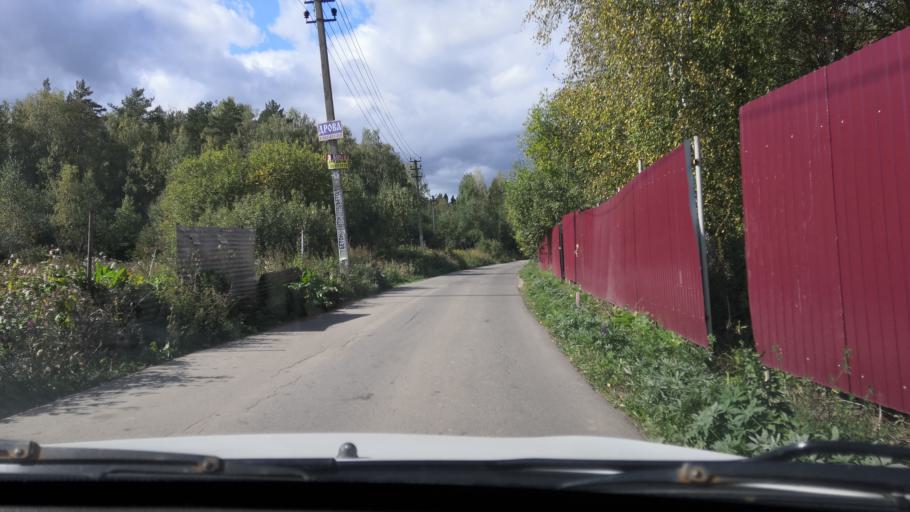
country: RU
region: Moskovskaya
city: Povarovo
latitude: 56.0646
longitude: 37.0396
